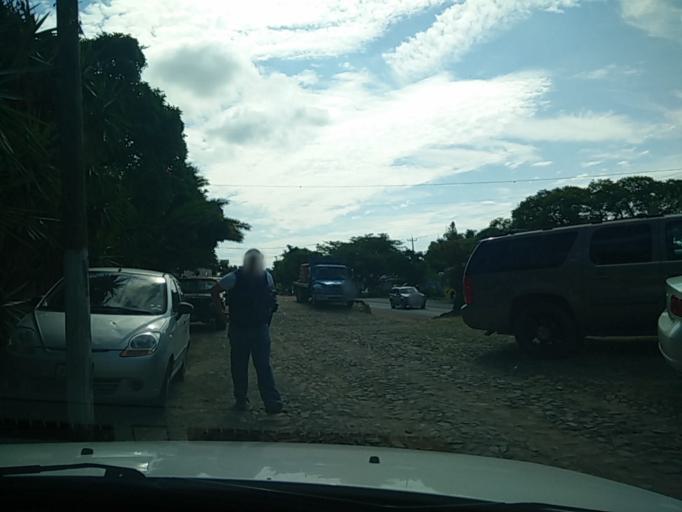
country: MX
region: Jalisco
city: Ajijic
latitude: 20.3008
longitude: -103.2584
